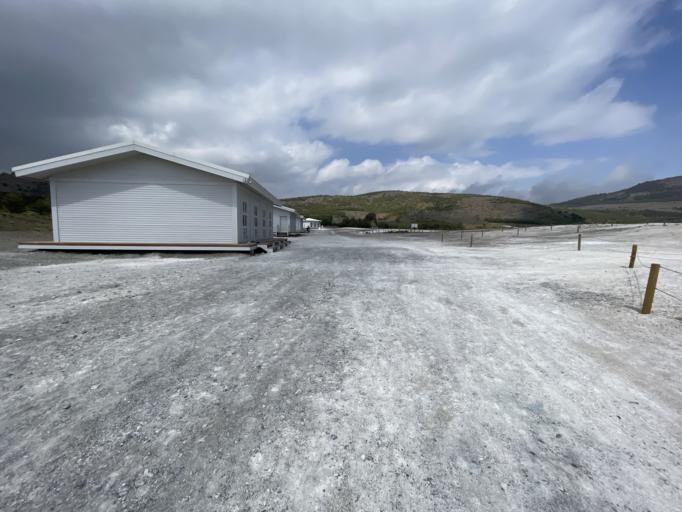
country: TR
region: Burdur
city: Yesilova
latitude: 37.5333
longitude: 29.6442
